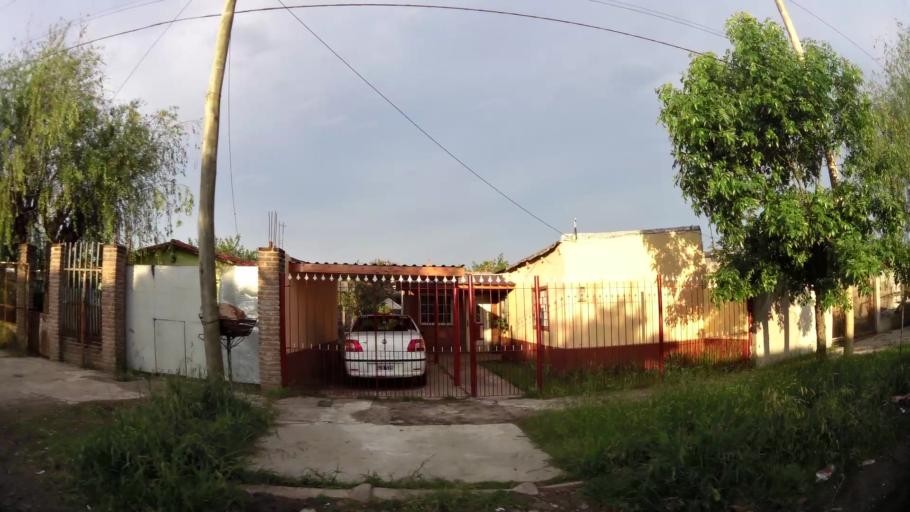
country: AR
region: Buenos Aires
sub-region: Partido de Almirante Brown
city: Adrogue
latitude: -34.7705
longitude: -58.3422
